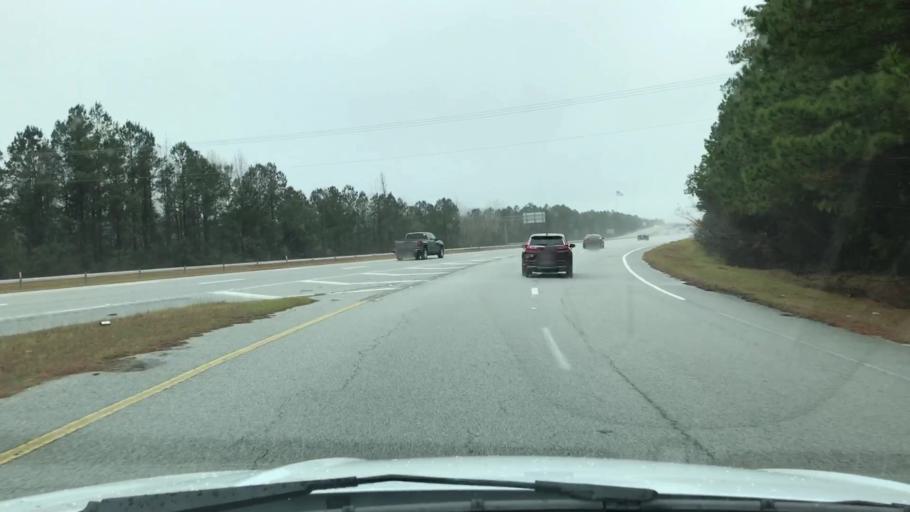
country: US
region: South Carolina
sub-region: Horry County
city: Myrtle Beach
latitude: 33.7527
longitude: -78.8593
